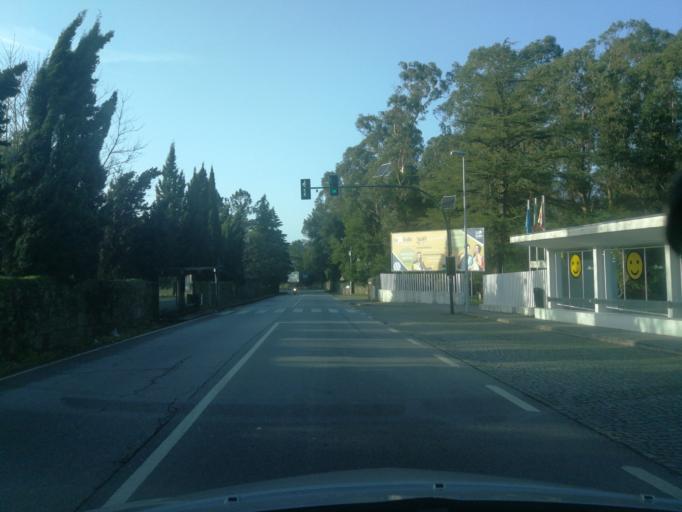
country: PT
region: Braga
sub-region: Barcelos
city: Barcelos
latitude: 41.5243
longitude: -8.6132
